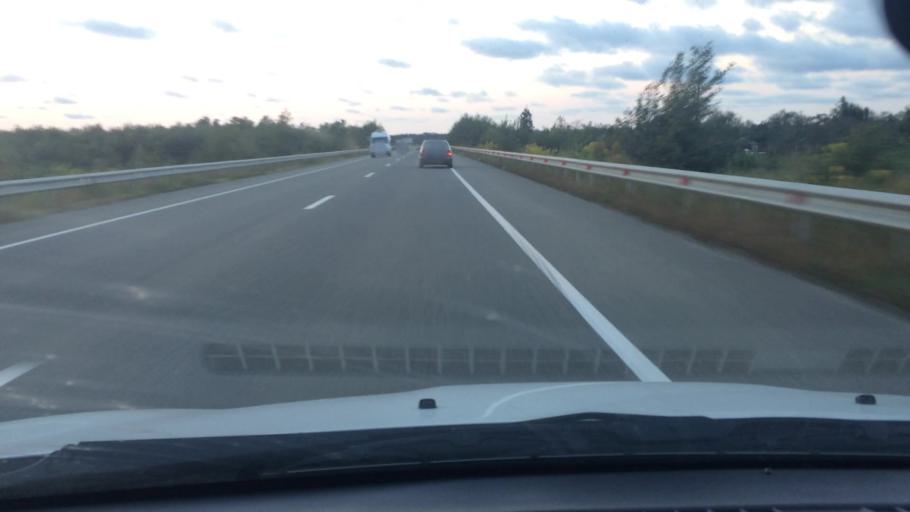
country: GE
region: Ajaria
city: Ochkhamuri
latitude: 41.9072
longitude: 41.7866
